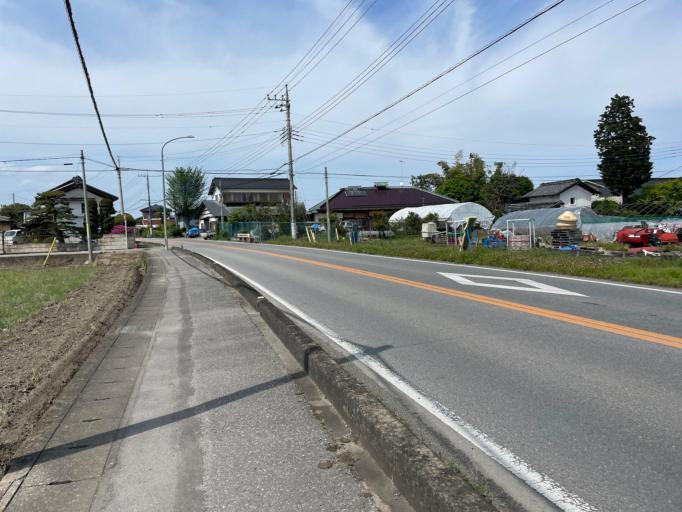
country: JP
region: Tochigi
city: Mibu
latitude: 36.4765
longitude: 139.7645
